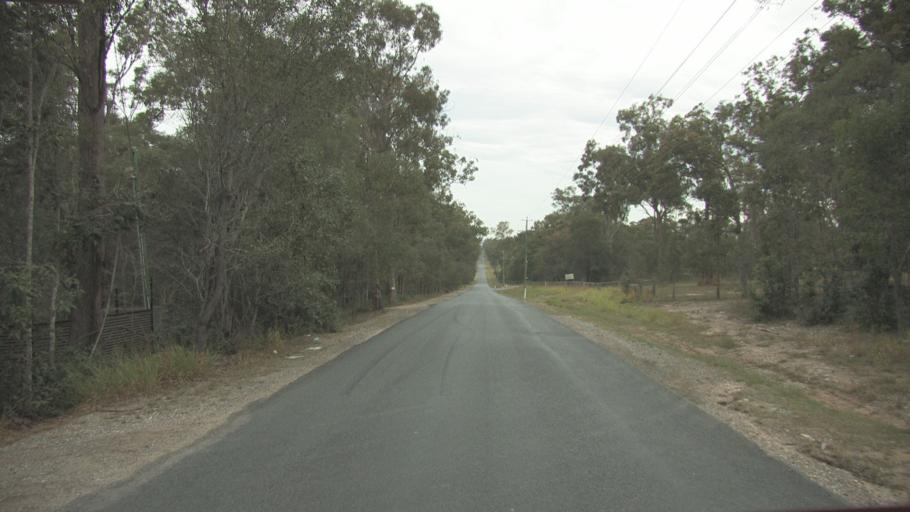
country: AU
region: Queensland
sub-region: Logan
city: Chambers Flat
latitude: -27.7832
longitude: 153.1192
